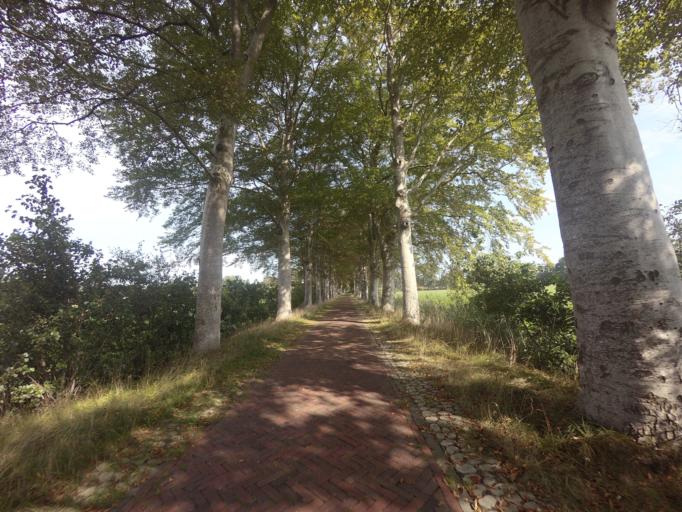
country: NL
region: Groningen
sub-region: Gemeente Leek
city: Leek
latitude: 53.1774
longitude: 6.3922
